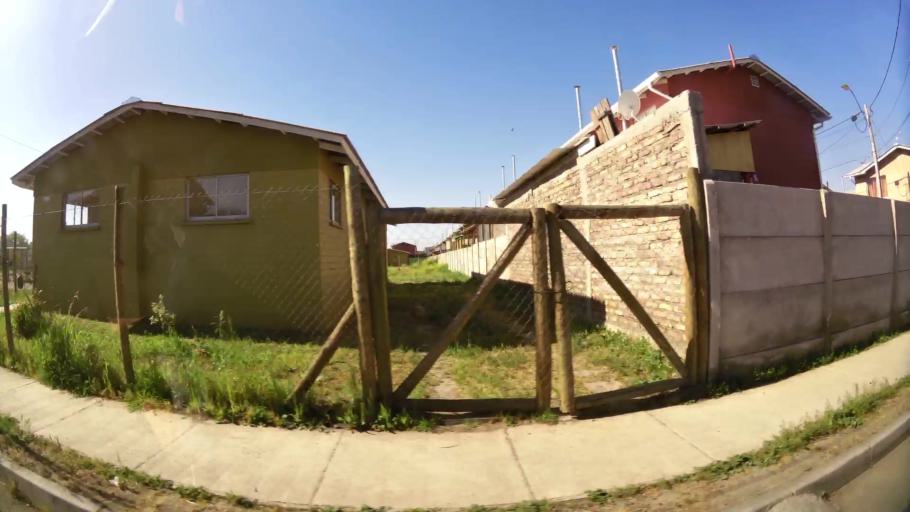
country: CL
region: Santiago Metropolitan
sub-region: Provincia de Talagante
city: Penaflor
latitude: -33.6169
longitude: -70.8803
